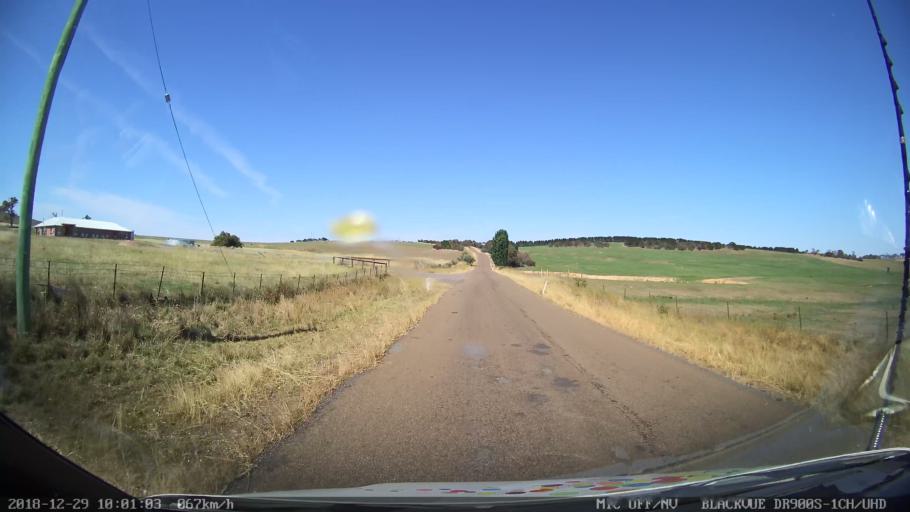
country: AU
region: New South Wales
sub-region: Goulburn Mulwaree
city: Goulburn
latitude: -34.7969
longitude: 149.4808
